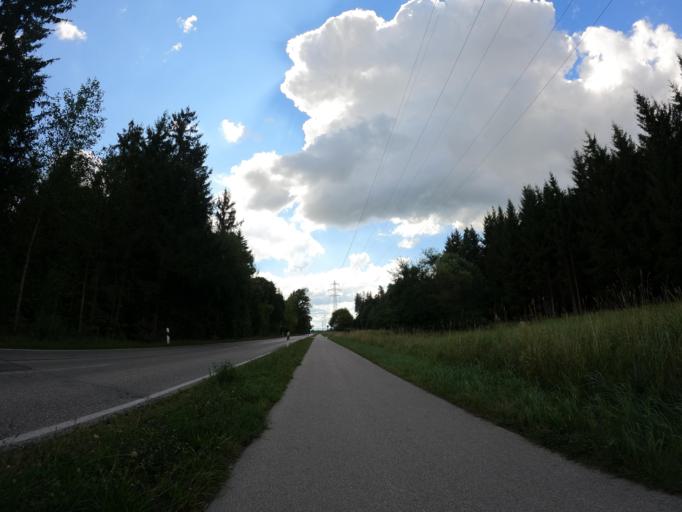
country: DE
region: Bavaria
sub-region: Upper Bavaria
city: Brunnthal
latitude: 48.0205
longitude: 11.6822
